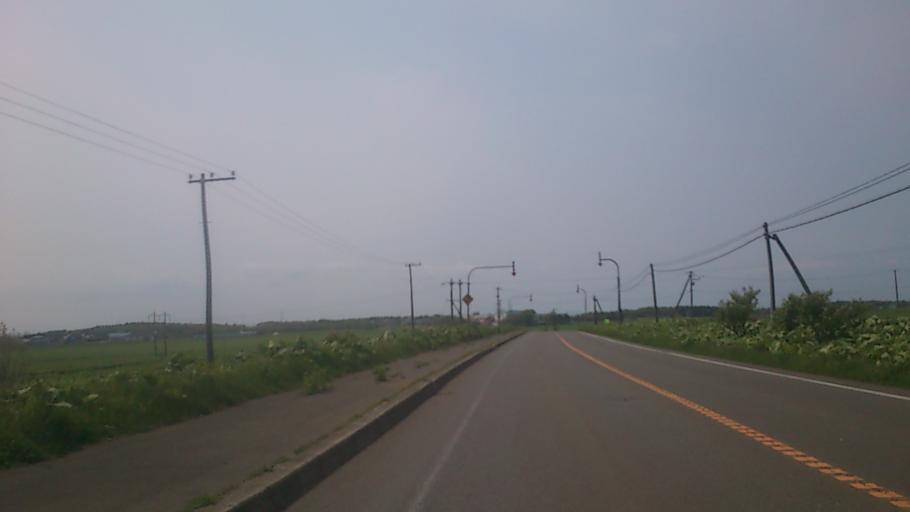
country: JP
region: Hokkaido
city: Nemuro
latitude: 43.2748
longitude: 145.5285
